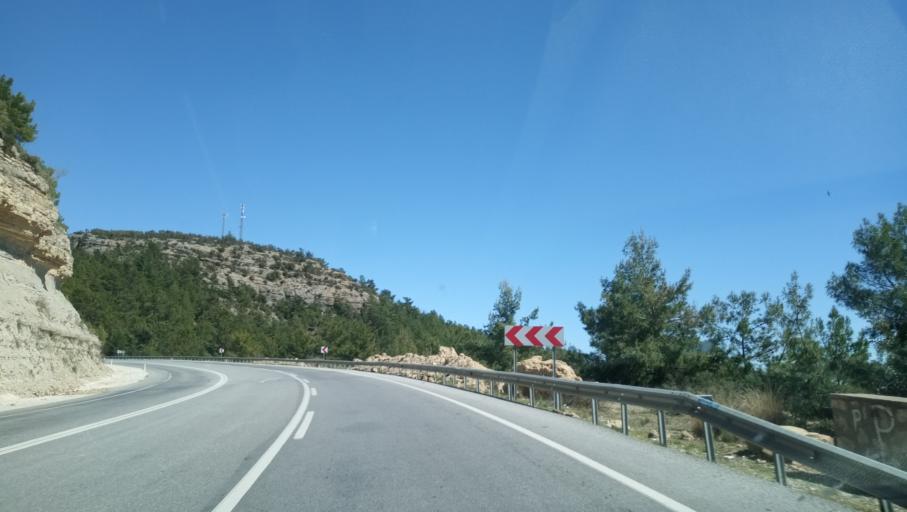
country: TR
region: Antalya
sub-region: Alanya
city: Okurcalar
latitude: 36.7653
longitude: 31.6595
